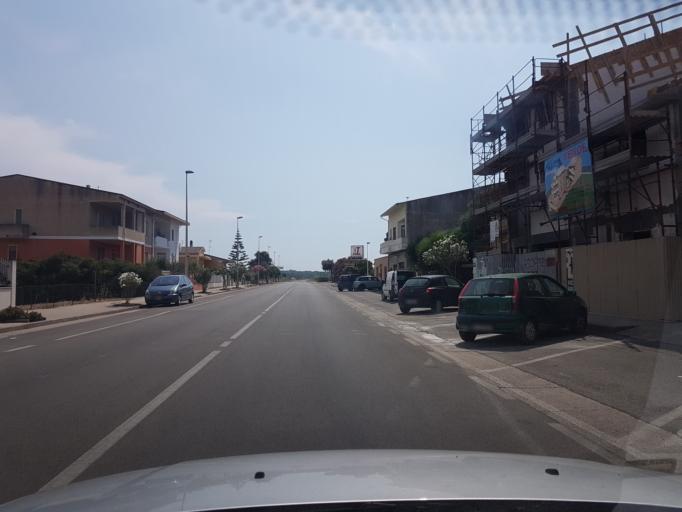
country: IT
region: Sardinia
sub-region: Provincia di Oristano
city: Cabras
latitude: 39.9220
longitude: 8.5235
